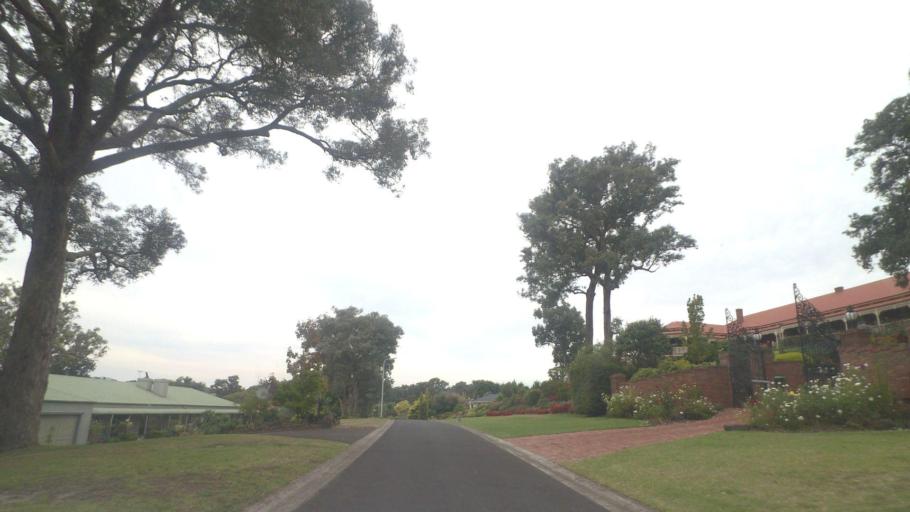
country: AU
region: Victoria
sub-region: Nillumbik
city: Eltham
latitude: -37.7450
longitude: 145.1798
